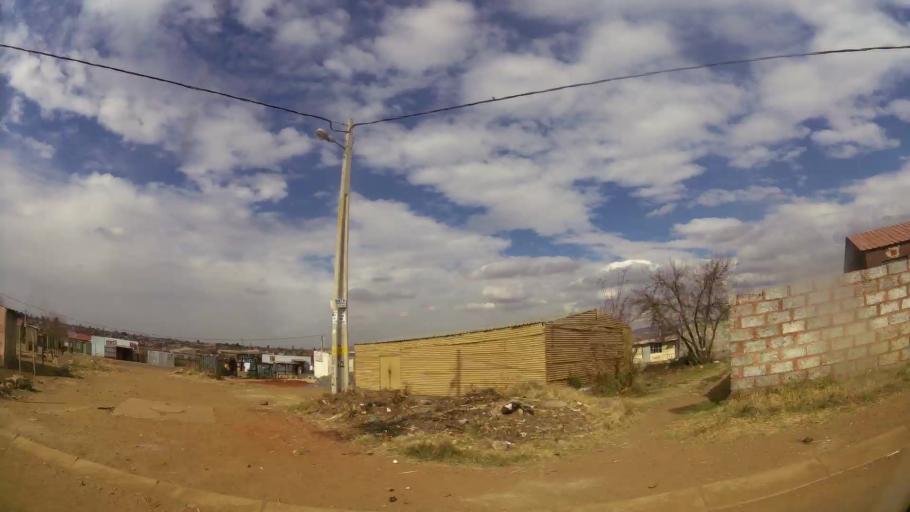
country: ZA
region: Gauteng
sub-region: Ekurhuleni Metropolitan Municipality
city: Germiston
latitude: -26.4134
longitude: 28.1648
